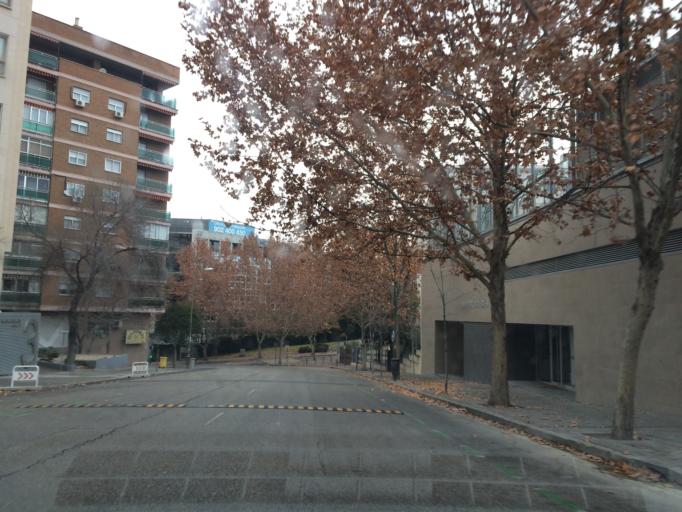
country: ES
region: Madrid
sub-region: Provincia de Madrid
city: Chamberi
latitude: 40.4472
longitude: -3.7142
